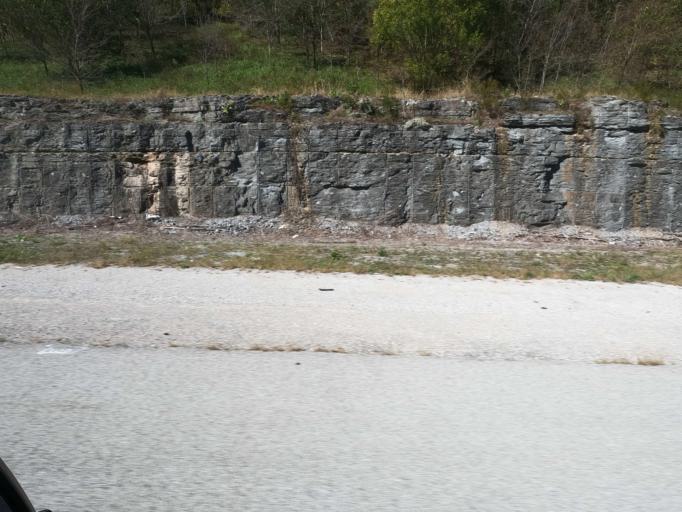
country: US
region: Tennessee
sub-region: Maury County
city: Mount Pleasant
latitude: 35.4756
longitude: -87.2621
